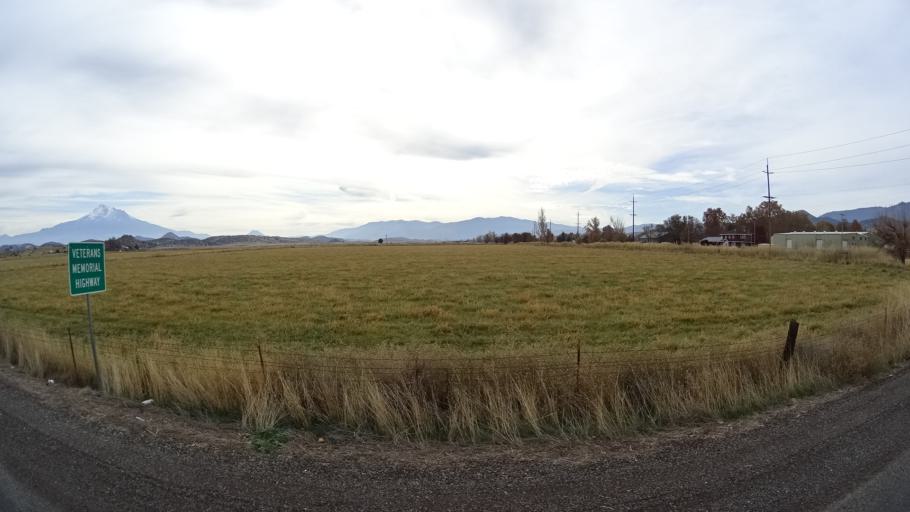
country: US
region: California
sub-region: Siskiyou County
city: Montague
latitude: 41.6472
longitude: -122.5196
